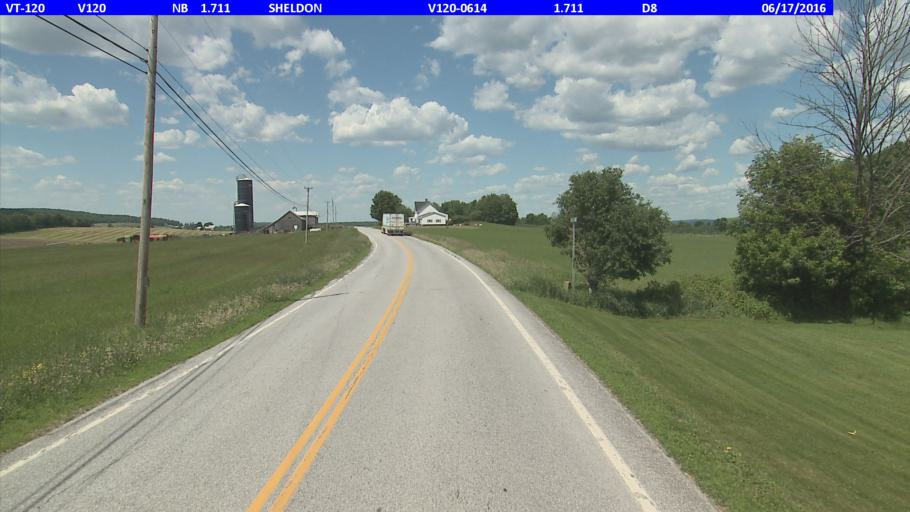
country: US
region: Vermont
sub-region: Franklin County
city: Enosburg Falls
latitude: 44.9344
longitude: -72.8997
